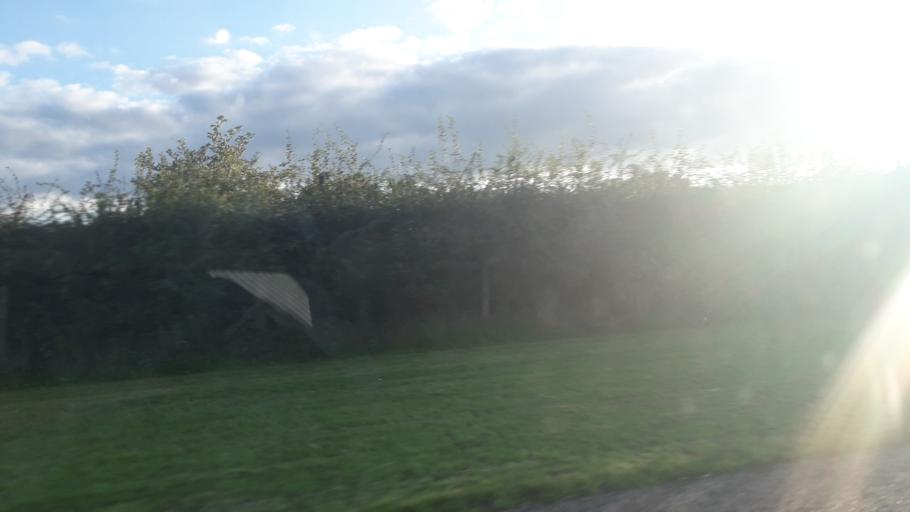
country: IE
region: Leinster
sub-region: Lu
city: Blackrock
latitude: 54.0102
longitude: -6.2999
